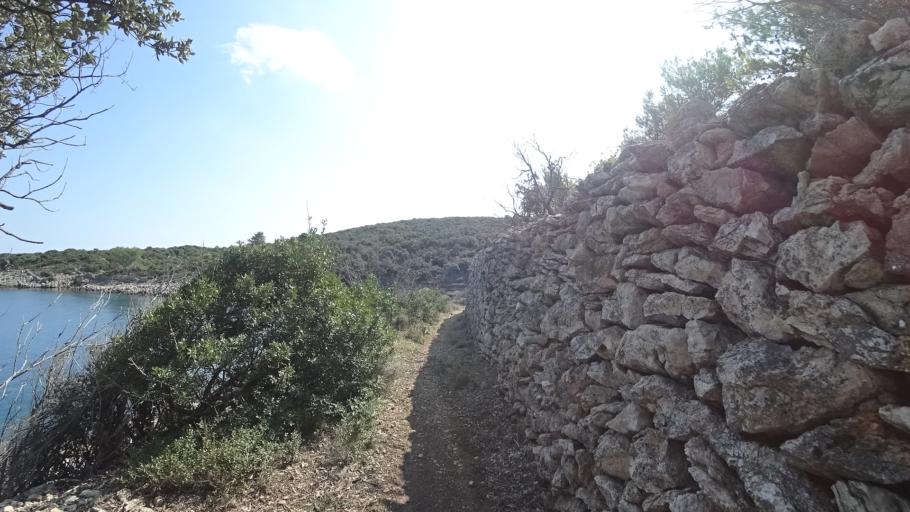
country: HR
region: Primorsko-Goranska
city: Mali Losinj
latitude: 44.5031
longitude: 14.5237
